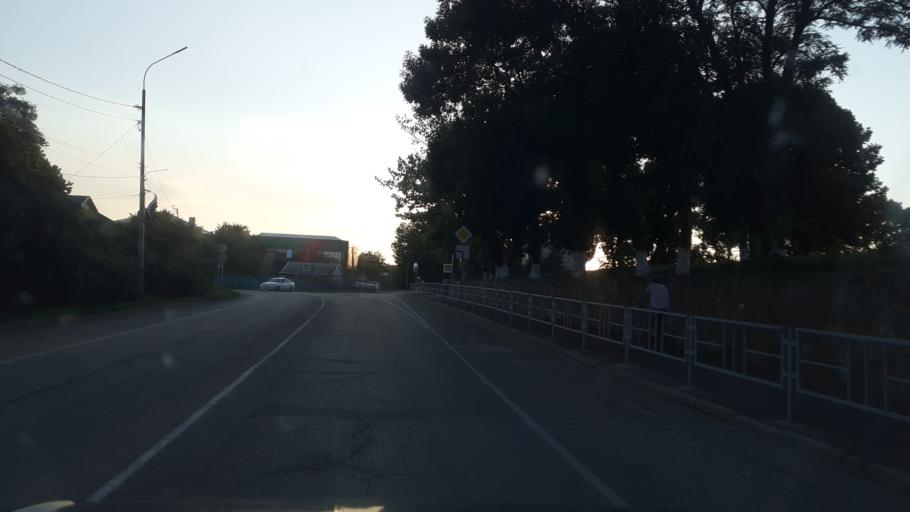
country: RU
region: Krasnodarskiy
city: Severskaya
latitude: 44.8446
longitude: 38.6738
